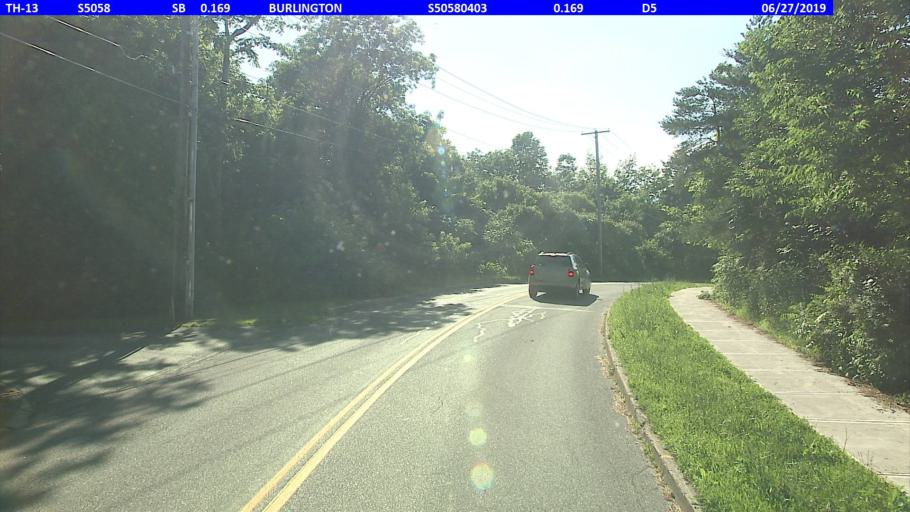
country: US
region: Vermont
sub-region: Chittenden County
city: Burlington
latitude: 44.4625
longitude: -73.2046
